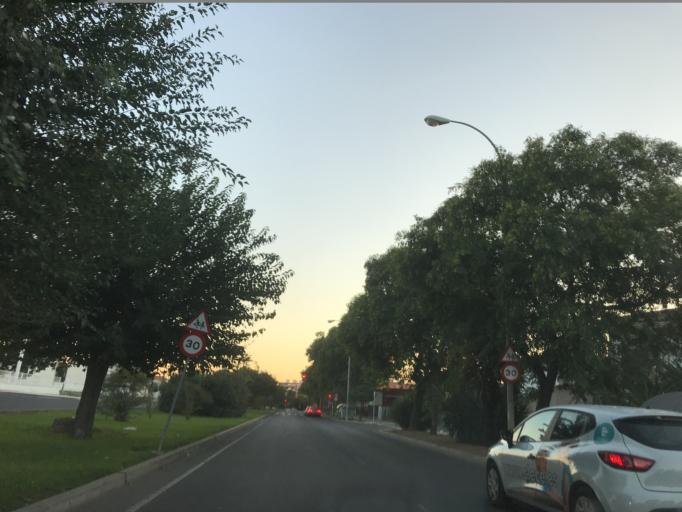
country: ES
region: Andalusia
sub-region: Provincia de Sevilla
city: Sevilla
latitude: 37.3887
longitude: -5.9153
